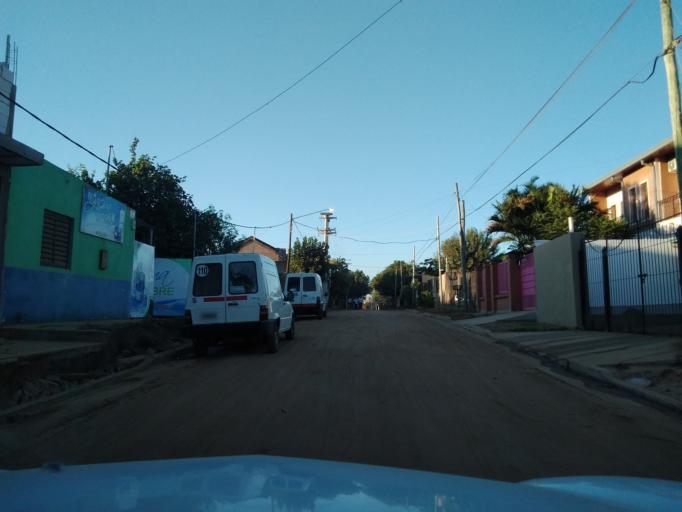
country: AR
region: Corrientes
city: Corrientes
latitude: -27.4772
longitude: -58.7880
